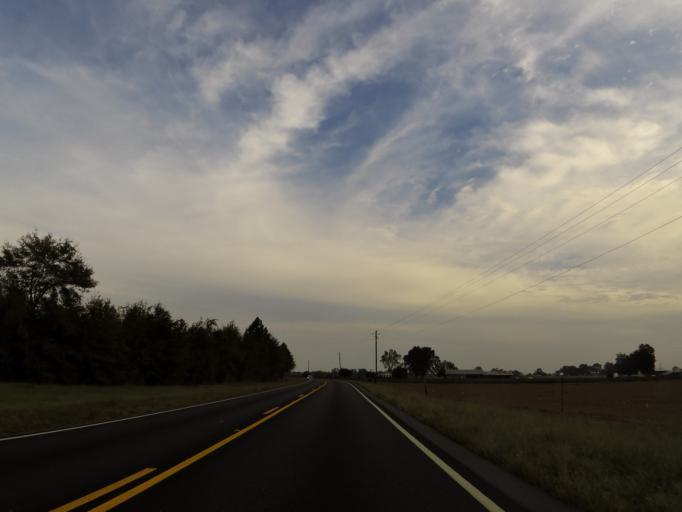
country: US
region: Alabama
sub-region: Escambia County
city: Atmore
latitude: 31.2299
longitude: -87.4797
